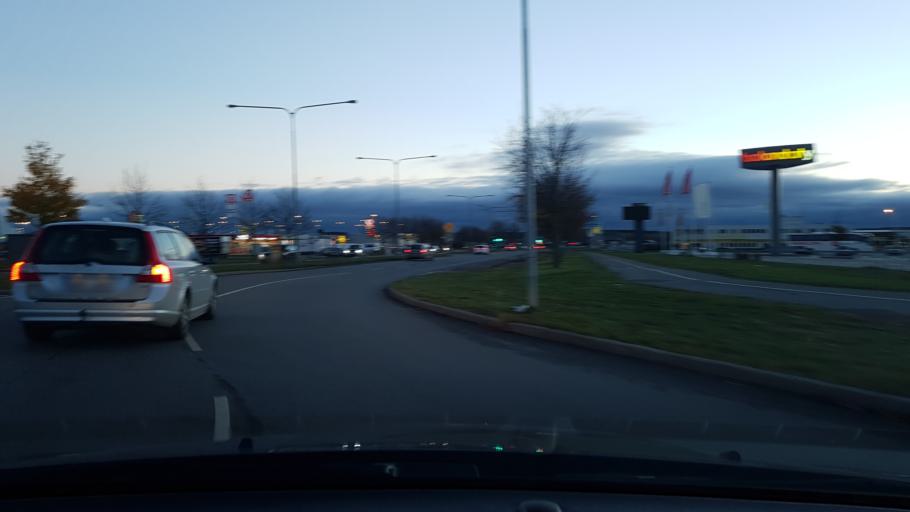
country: SE
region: Uppsala
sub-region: Uppsala Kommun
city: Saevja
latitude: 59.8474
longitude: 17.6900
